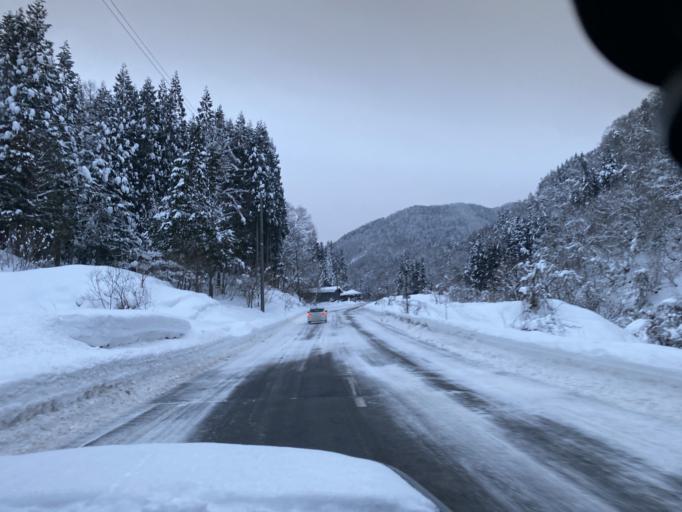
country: JP
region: Nagano
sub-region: Kitaazumi Gun
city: Hakuba
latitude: 36.6009
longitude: 137.8888
